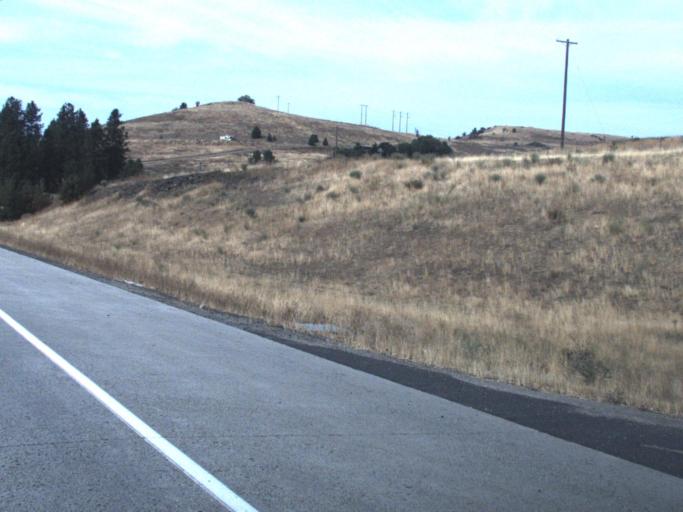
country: US
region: Washington
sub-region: Adams County
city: Ritzville
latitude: 47.1086
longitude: -118.3980
